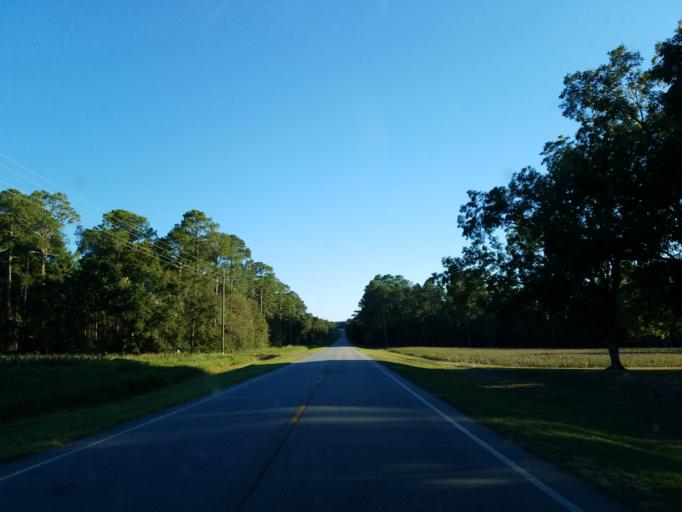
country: US
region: Georgia
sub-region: Worth County
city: Sylvester
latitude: 31.6056
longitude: -83.8644
